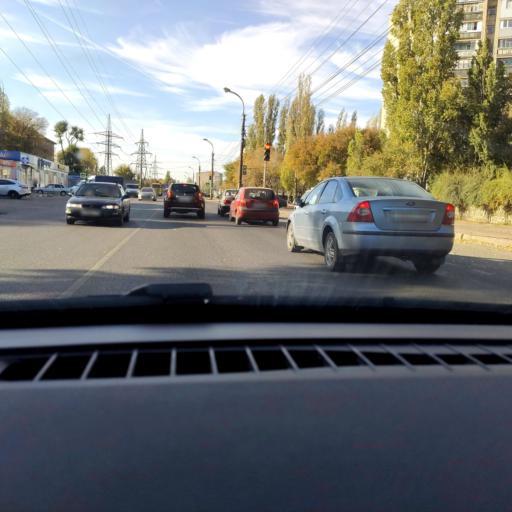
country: RU
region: Voronezj
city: Voronezh
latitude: 51.6408
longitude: 39.1591
